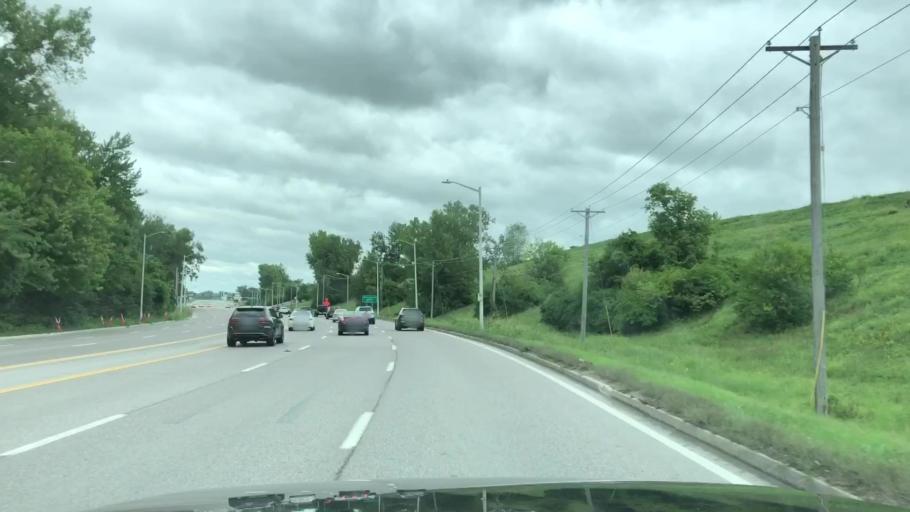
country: US
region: Missouri
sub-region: Saint Charles County
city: Saint Charles
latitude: 38.7454
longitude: -90.4651
